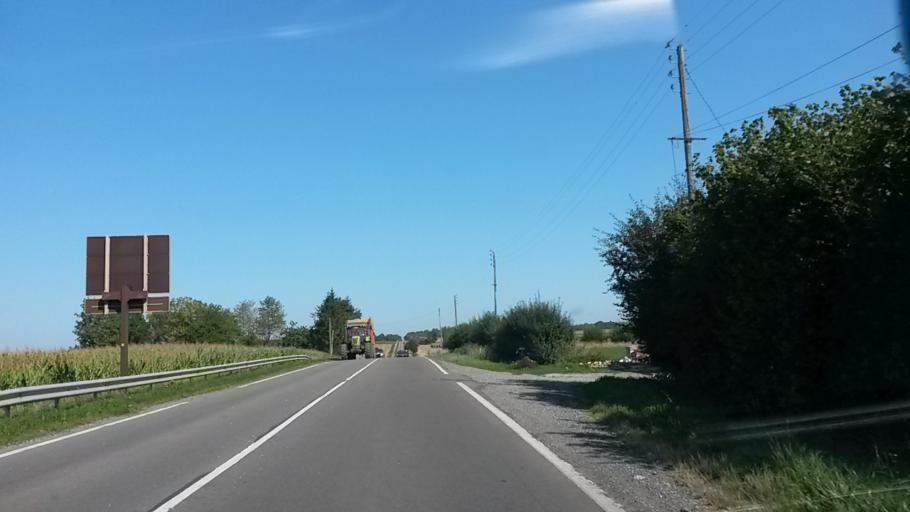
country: FR
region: Nord-Pas-de-Calais
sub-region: Departement du Nord
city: Avesnelles
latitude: 50.1791
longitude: 3.9525
